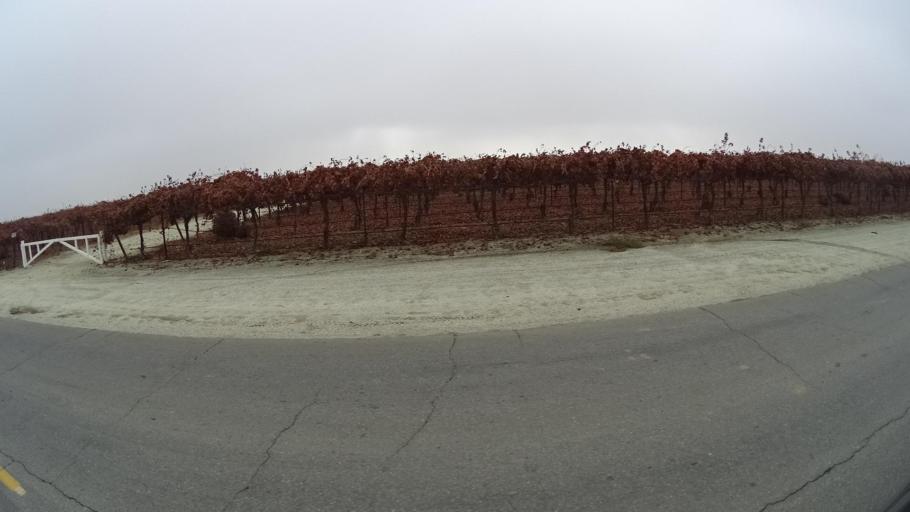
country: US
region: California
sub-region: Kern County
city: Greenfield
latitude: 35.0944
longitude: -119.1251
